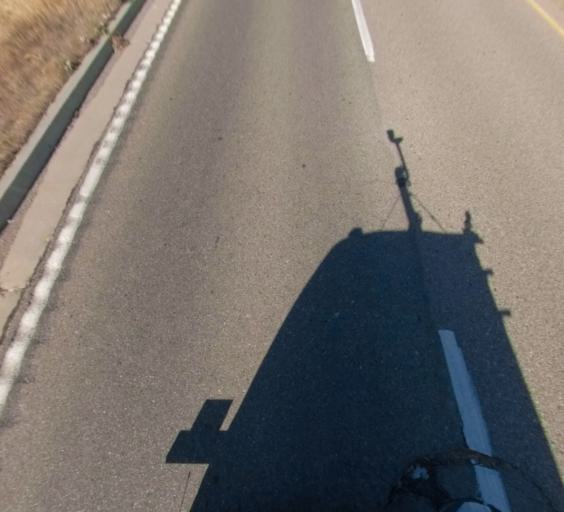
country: US
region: California
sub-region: Fresno County
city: Clovis
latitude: 36.8912
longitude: -119.7972
